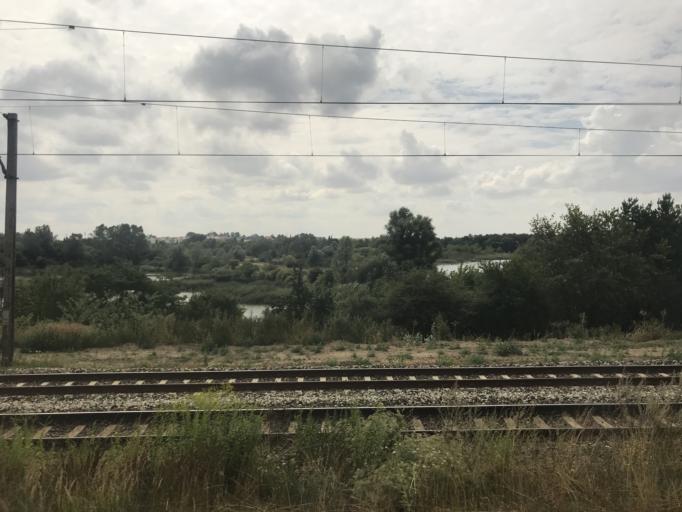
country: PL
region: Greater Poland Voivodeship
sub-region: Powiat gnieznienski
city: Gniezno
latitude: 52.5275
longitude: 17.5872
